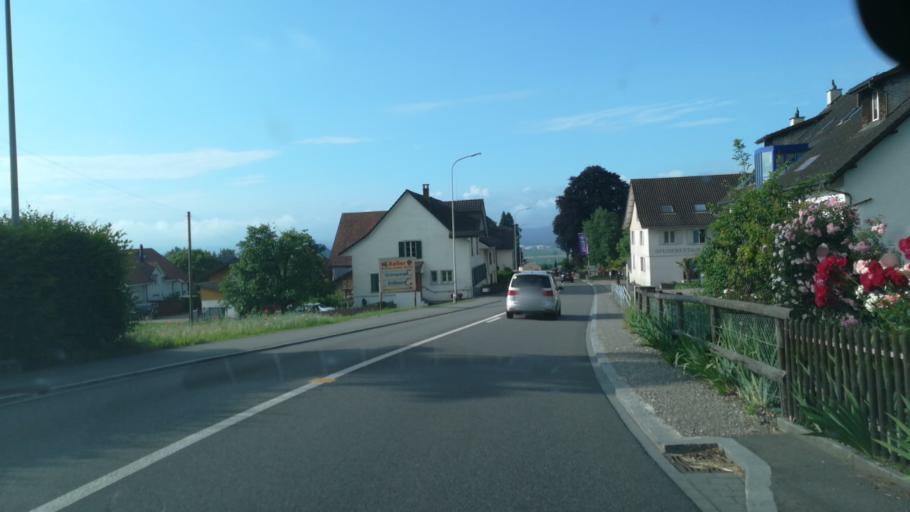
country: CH
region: Thurgau
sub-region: Weinfelden District
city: Berg
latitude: 47.5755
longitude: 9.1677
